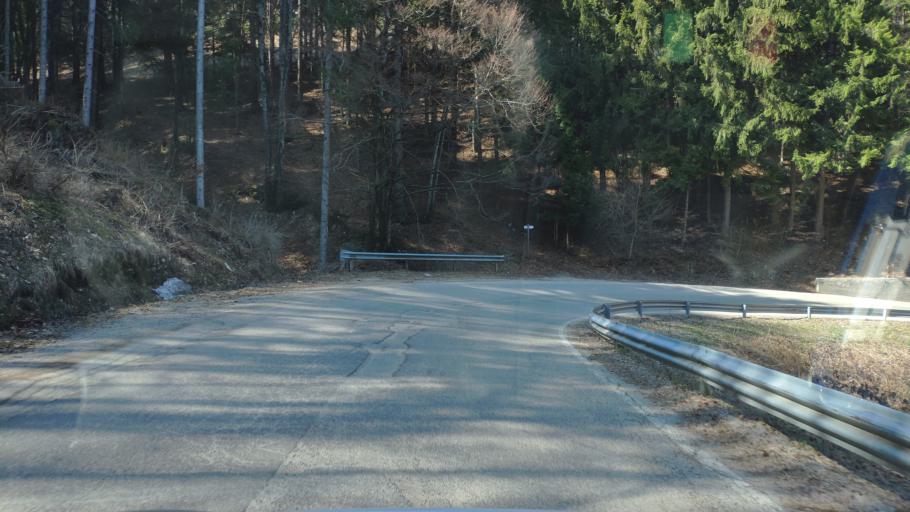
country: IT
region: Veneto
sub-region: Provincia di Vicenza
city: Enego
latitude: 45.9331
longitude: 11.7017
